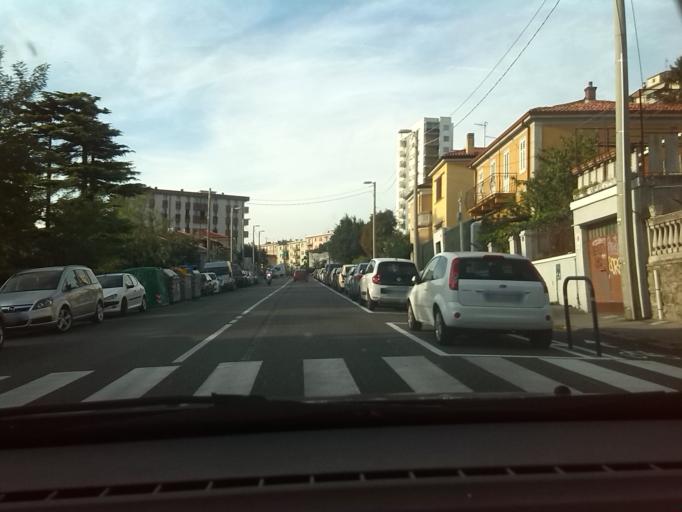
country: IT
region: Friuli Venezia Giulia
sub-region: Provincia di Trieste
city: Trieste
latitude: 45.6390
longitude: 13.7819
